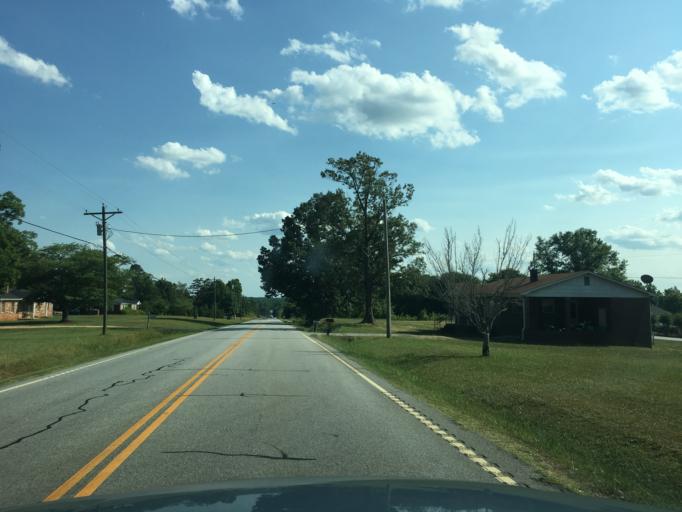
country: US
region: South Carolina
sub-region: Laurens County
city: Watts Mills
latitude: 34.5555
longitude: -81.9460
